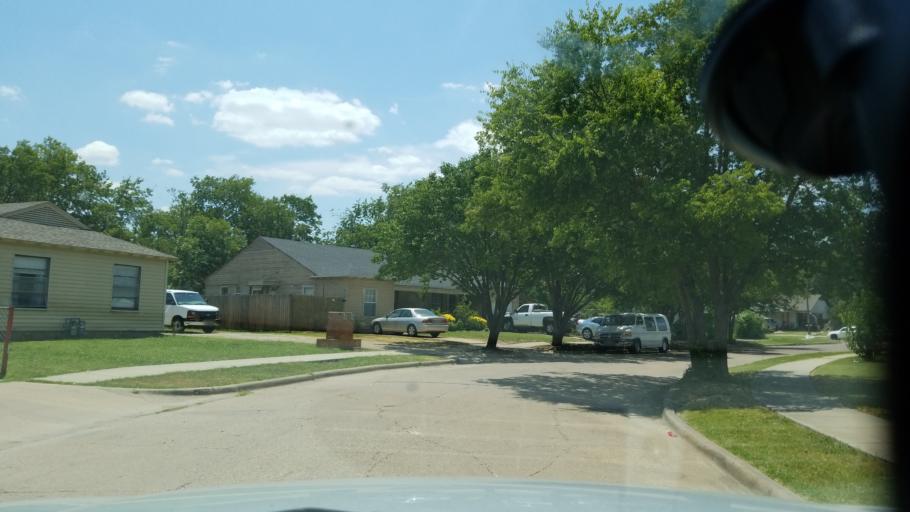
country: US
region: Texas
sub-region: Dallas County
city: Grand Prairie
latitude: 32.7508
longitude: -96.9738
